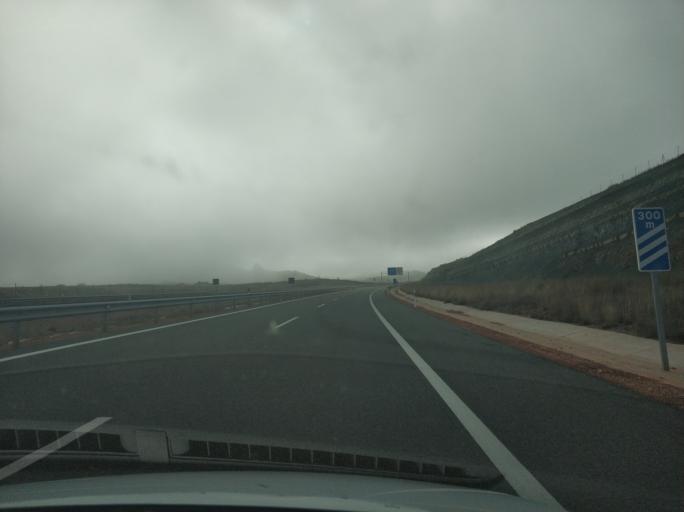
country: ES
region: Castille and Leon
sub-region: Provincia de Soria
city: Yelo
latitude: 41.2256
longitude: -2.4737
